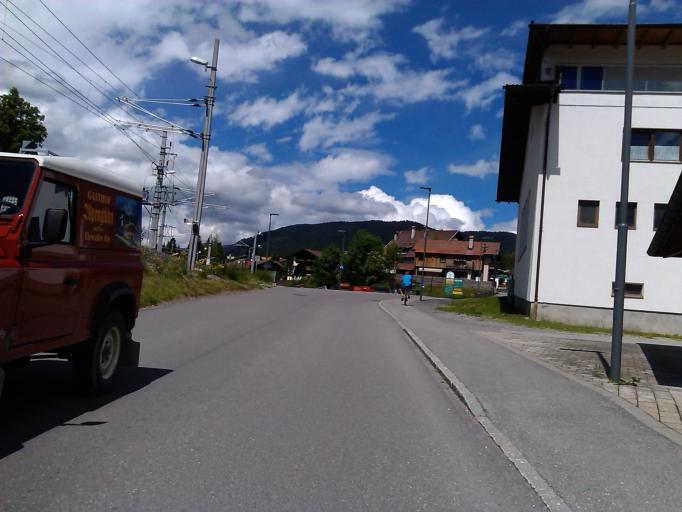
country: AT
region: Tyrol
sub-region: Politischer Bezirk Reutte
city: Ehrwald
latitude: 47.4084
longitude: 10.9132
